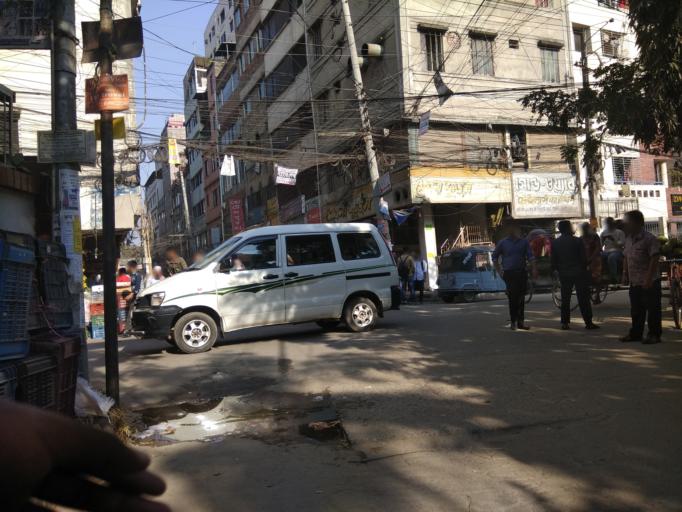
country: BD
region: Dhaka
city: Azimpur
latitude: 23.7740
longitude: 90.3652
